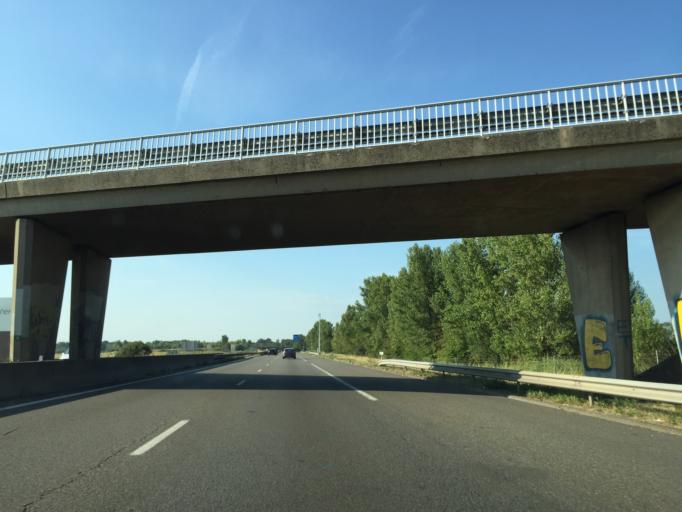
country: FR
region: Alsace
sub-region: Departement du Bas-Rhin
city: Reichstett
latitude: 48.6662
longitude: 7.7369
